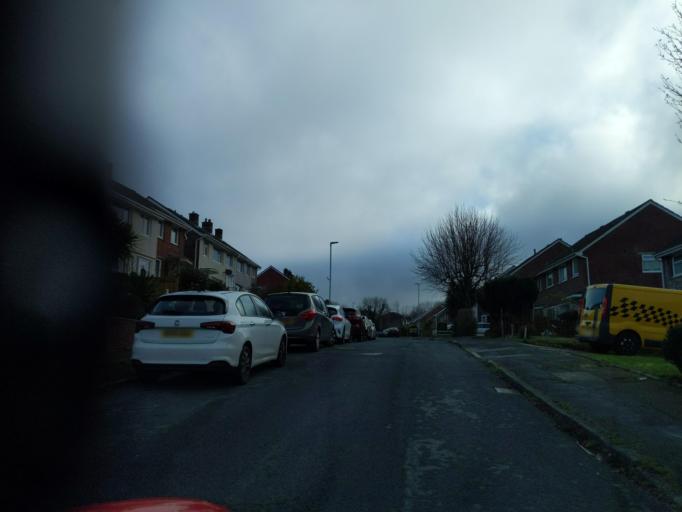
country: GB
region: England
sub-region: Devon
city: Yelverton
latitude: 50.4347
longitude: -4.1180
